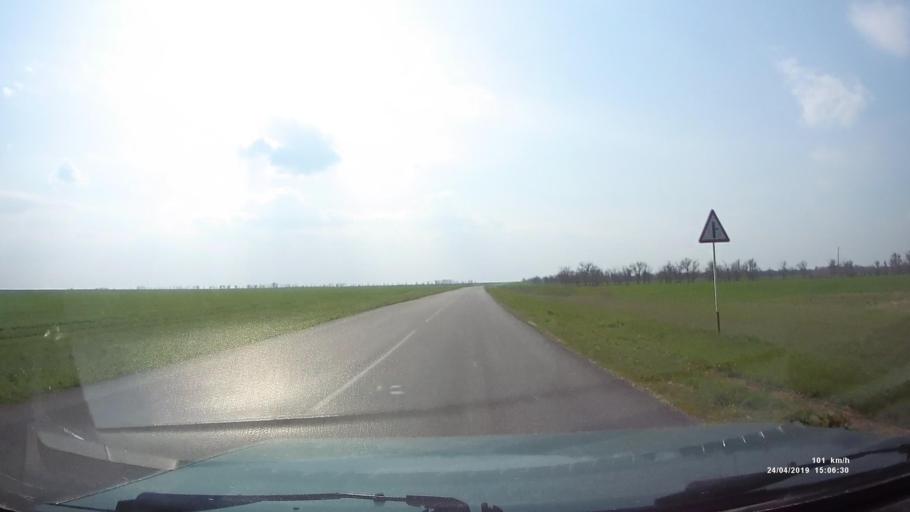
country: RU
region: Rostov
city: Remontnoye
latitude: 46.5588
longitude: 43.4259
